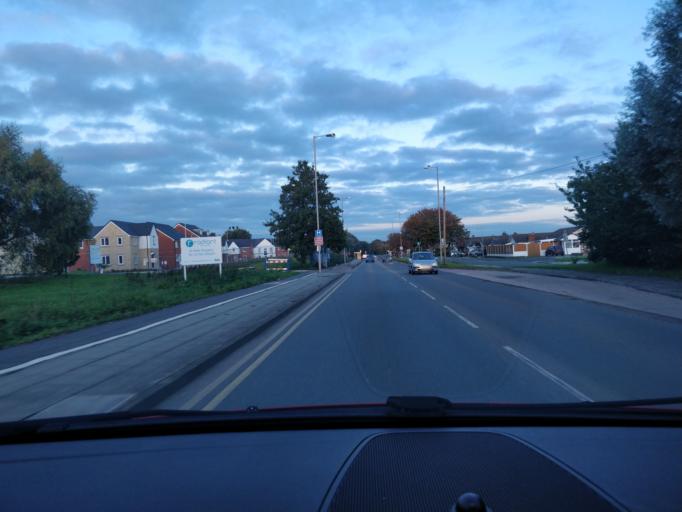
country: GB
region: England
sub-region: Sefton
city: Southport
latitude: 53.6313
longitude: -2.9835
